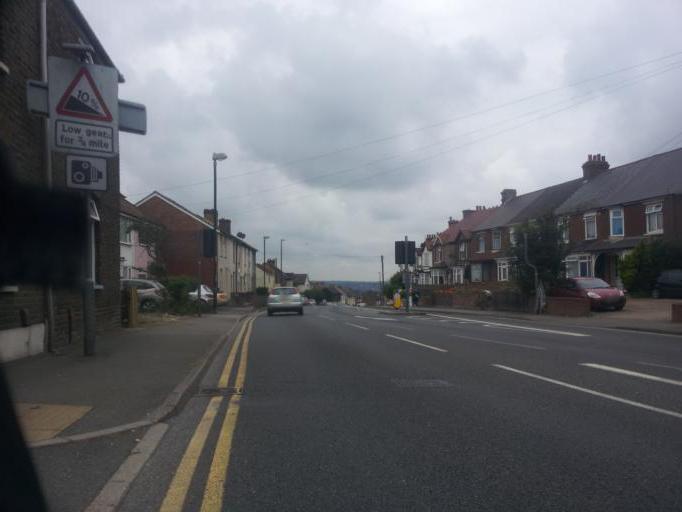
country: GB
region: England
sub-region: Kent
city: Gillingham
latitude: 51.3745
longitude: 0.5465
